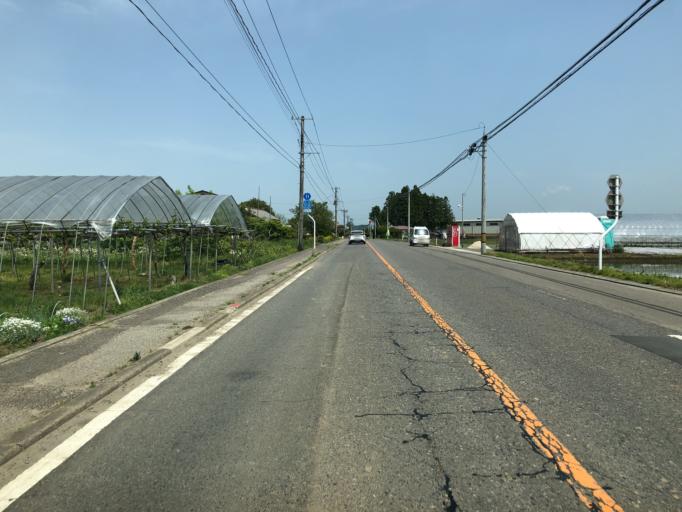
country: JP
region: Fukushima
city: Ishikawa
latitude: 37.1358
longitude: 140.3826
